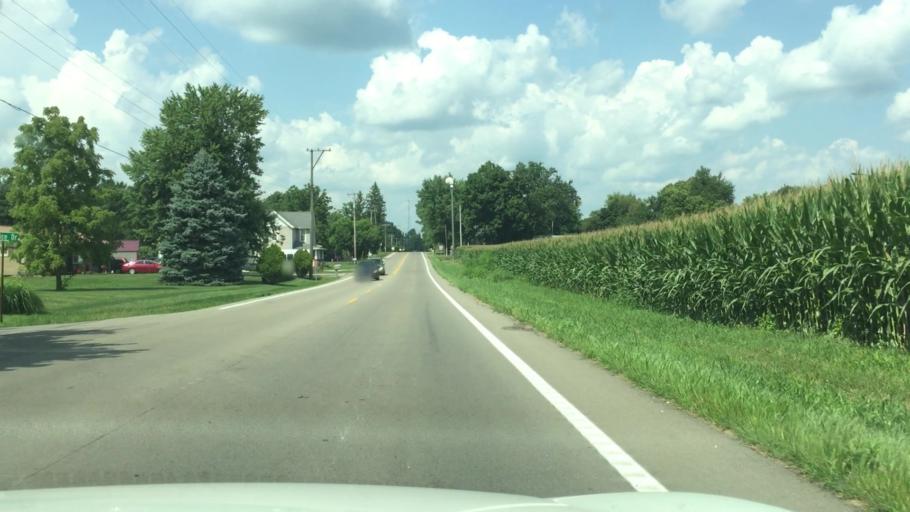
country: US
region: Ohio
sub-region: Clark County
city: Northridge
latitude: 39.9631
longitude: -83.7596
